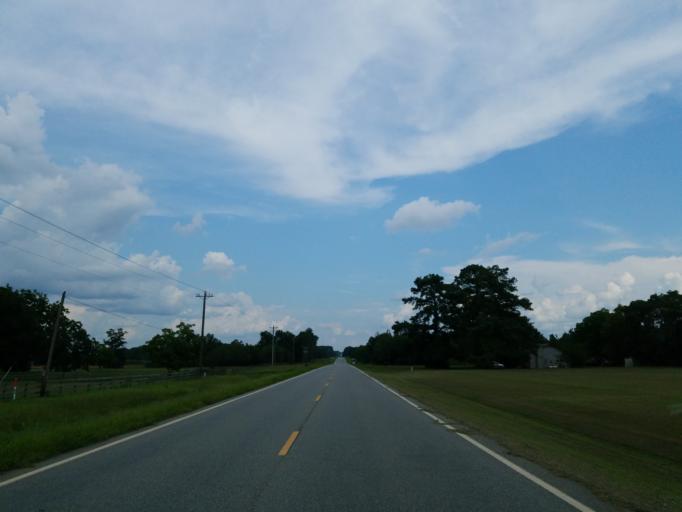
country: US
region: Georgia
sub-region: Dooly County
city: Unadilla
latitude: 32.3319
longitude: -83.7503
